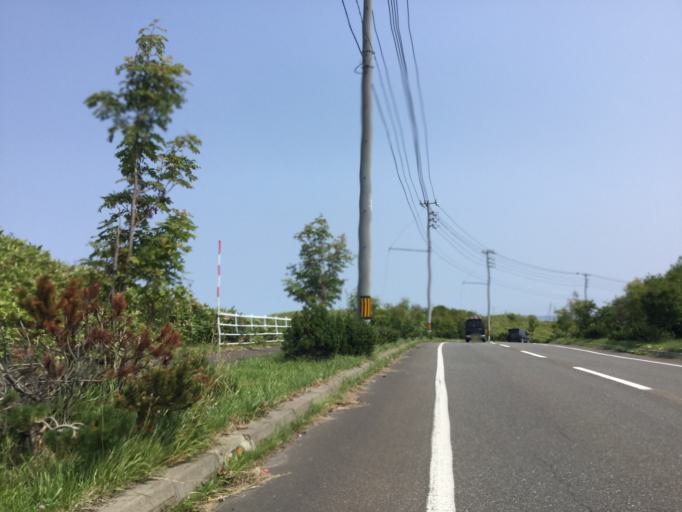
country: JP
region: Hokkaido
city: Wakkanai
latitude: 45.3863
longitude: 141.7290
